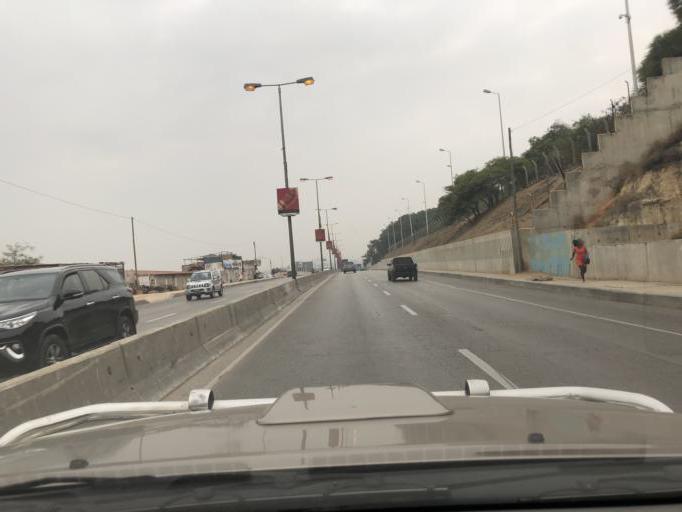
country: AO
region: Luanda
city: Luanda
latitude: -8.8641
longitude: 13.2018
